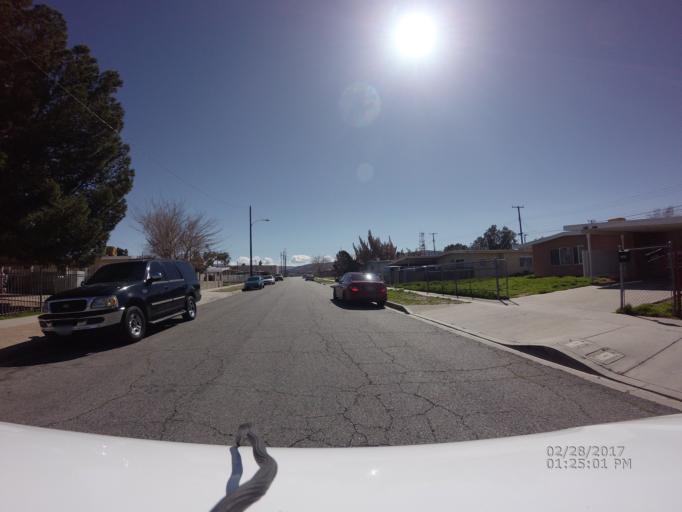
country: US
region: California
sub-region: Los Angeles County
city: Palmdale
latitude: 34.5888
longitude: -118.1156
